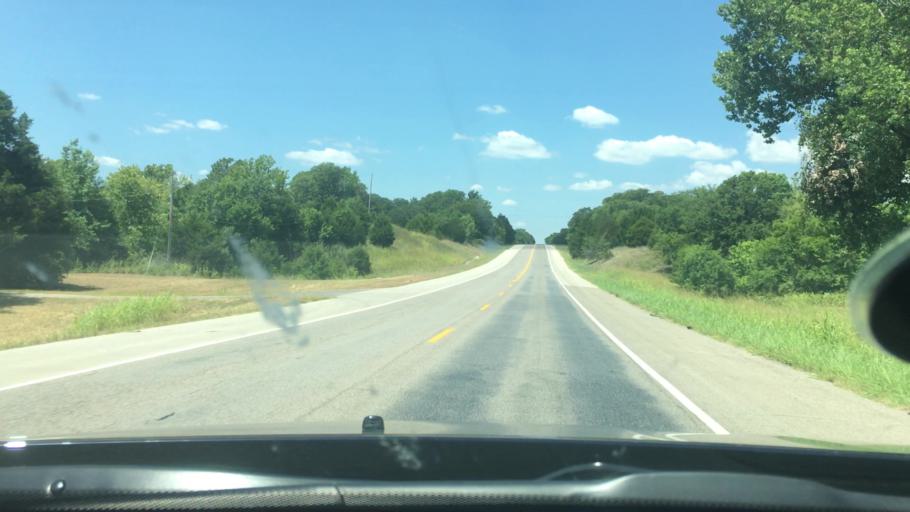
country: US
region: Oklahoma
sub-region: Carter County
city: Dickson
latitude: 34.1873
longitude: -96.9369
